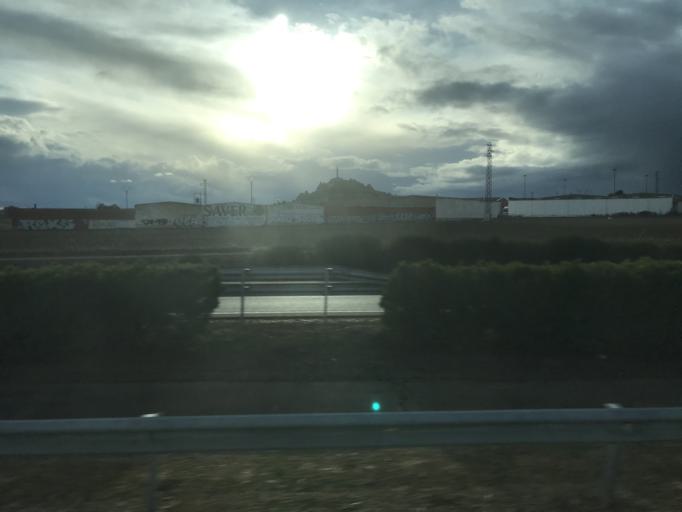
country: ES
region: Castille and Leon
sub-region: Provincia de Palencia
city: Villalobon
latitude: 42.0311
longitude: -4.5171
